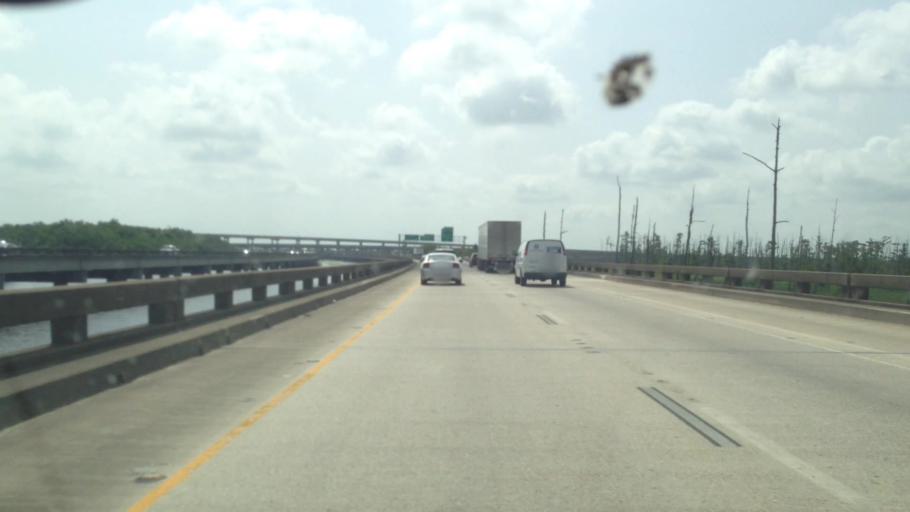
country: US
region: Louisiana
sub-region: Saint Charles Parish
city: Ama
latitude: 30.0087
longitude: -90.3016
